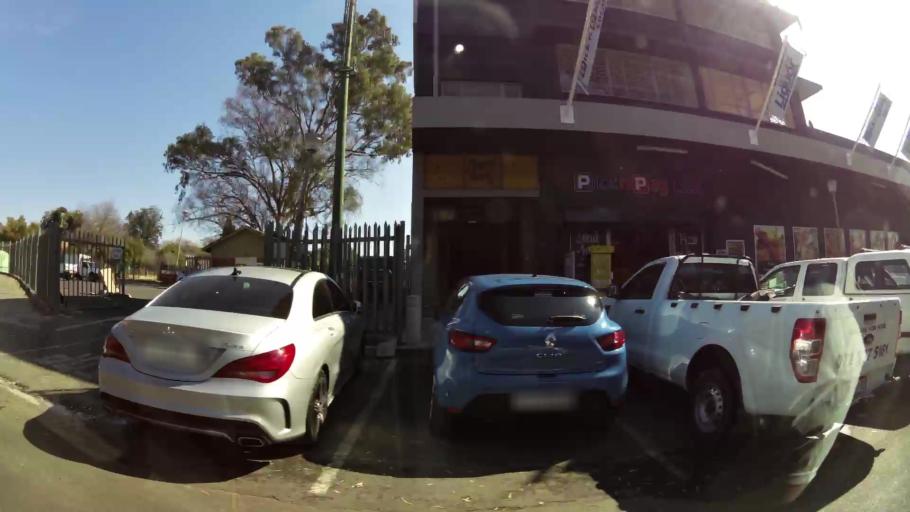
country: ZA
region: Gauteng
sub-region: City of Johannesburg Metropolitan Municipality
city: Modderfontein
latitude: -26.1580
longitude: 28.1243
